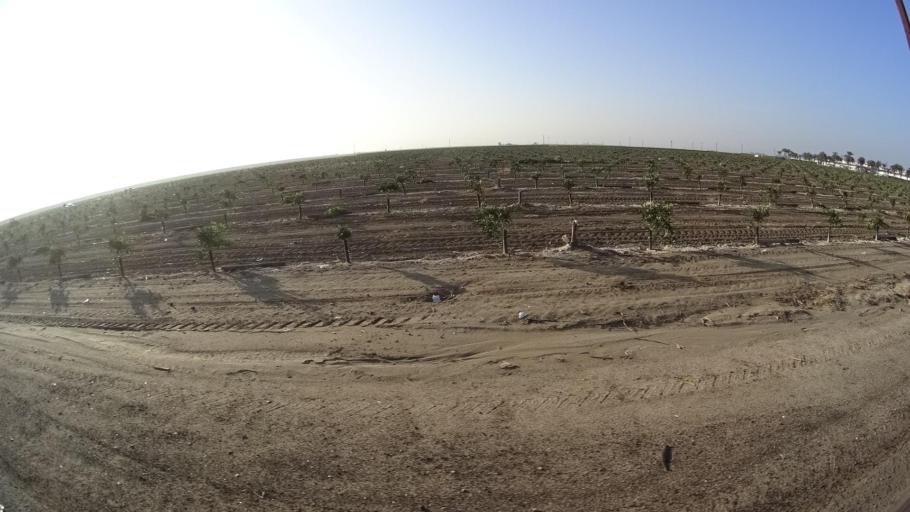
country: US
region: California
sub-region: Tulare County
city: Richgrove
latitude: 35.7906
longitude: -119.1576
